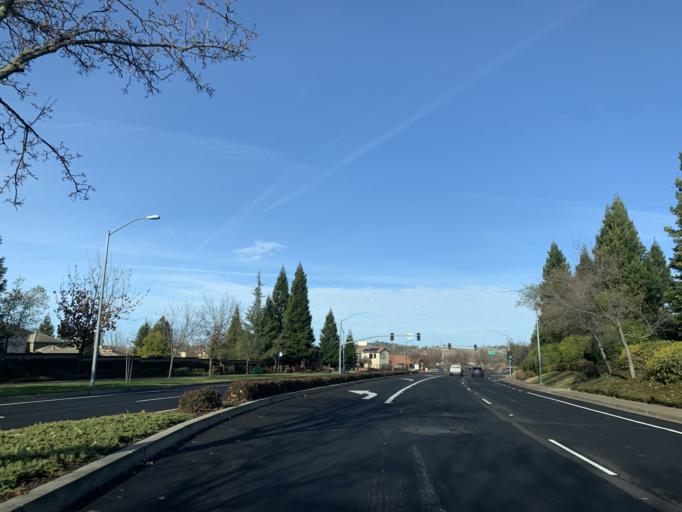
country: US
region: California
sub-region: El Dorado County
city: El Dorado Hills
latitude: 38.6764
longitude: -121.1081
